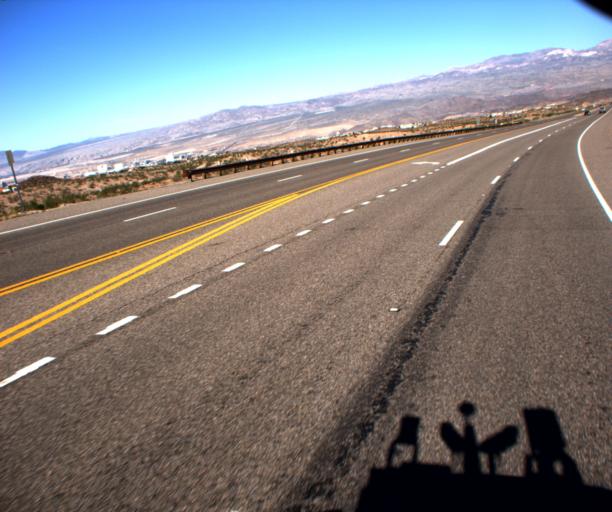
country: US
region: Nevada
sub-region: Clark County
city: Laughlin
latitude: 35.1849
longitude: -114.4983
